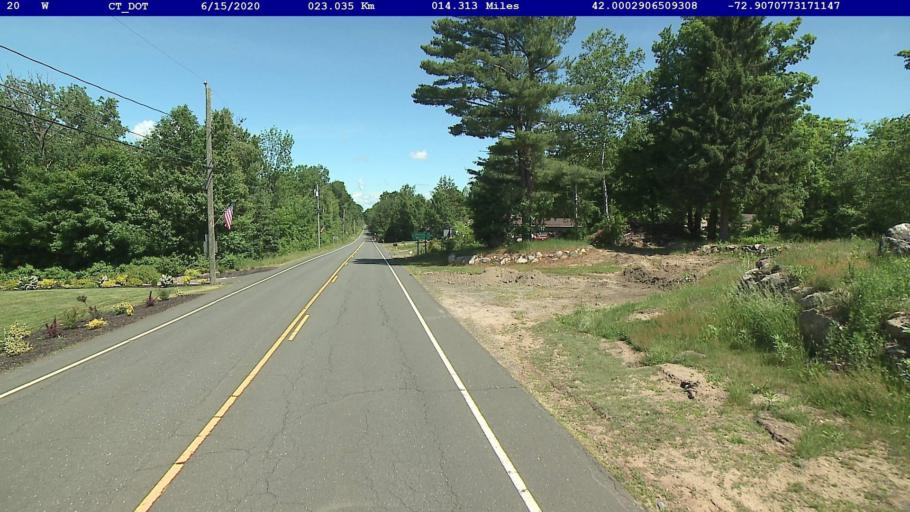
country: US
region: Connecticut
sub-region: Hartford County
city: North Granby
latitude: 42.0003
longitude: -72.9071
